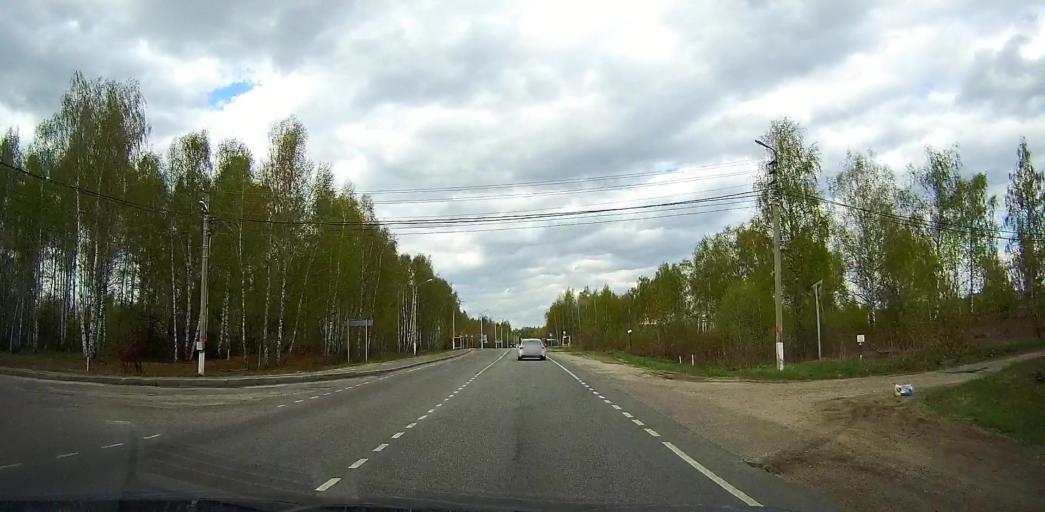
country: RU
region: Moskovskaya
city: Pavlovskiy Posad
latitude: 55.7580
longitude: 38.6560
